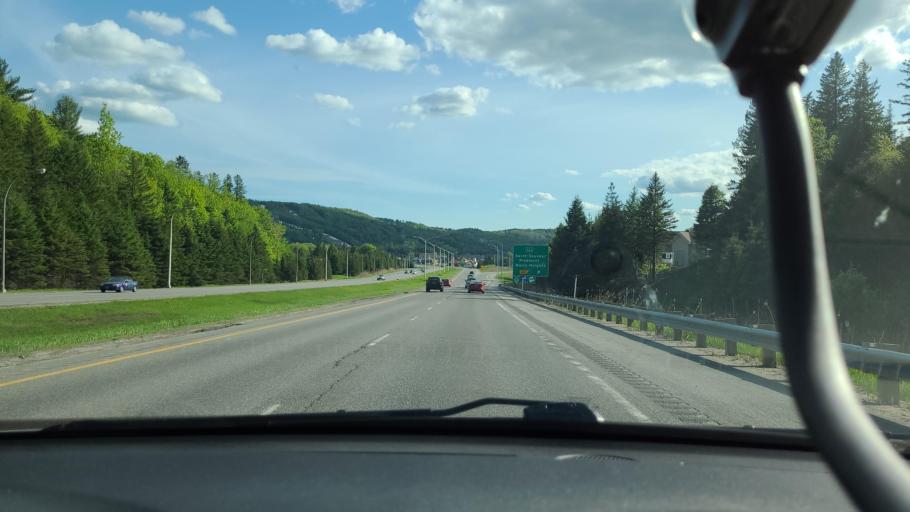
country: CA
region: Quebec
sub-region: Laurentides
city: Saint-Sauveur
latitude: 45.8999
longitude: -74.1435
